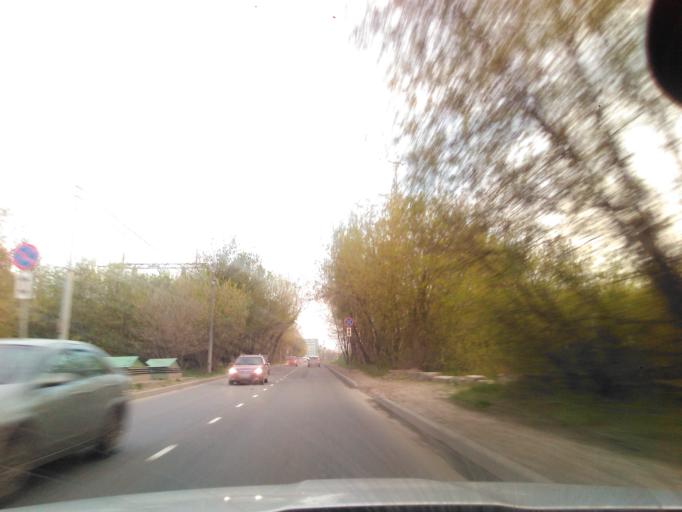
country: RU
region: Moscow
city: Kuz'minki
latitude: 55.6709
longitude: 37.8077
